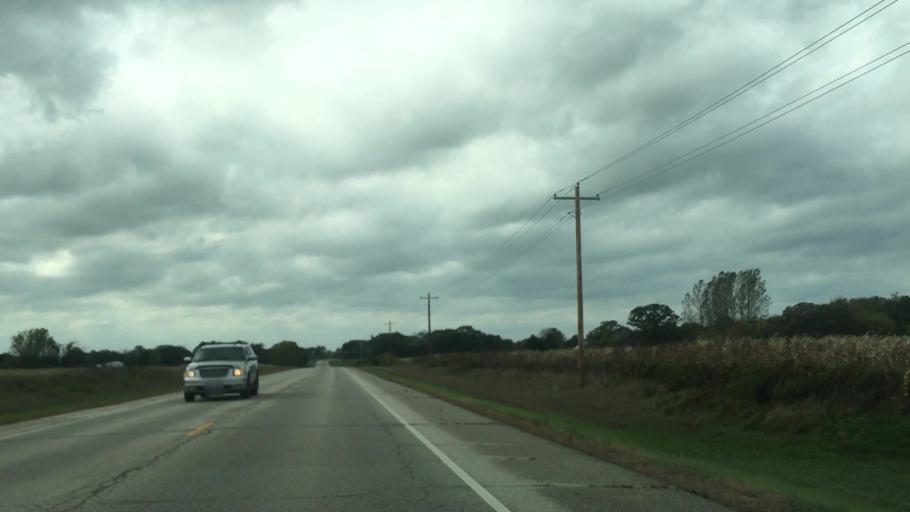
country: US
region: Minnesota
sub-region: Olmsted County
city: Eyota
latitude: 43.9344
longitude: -92.3211
